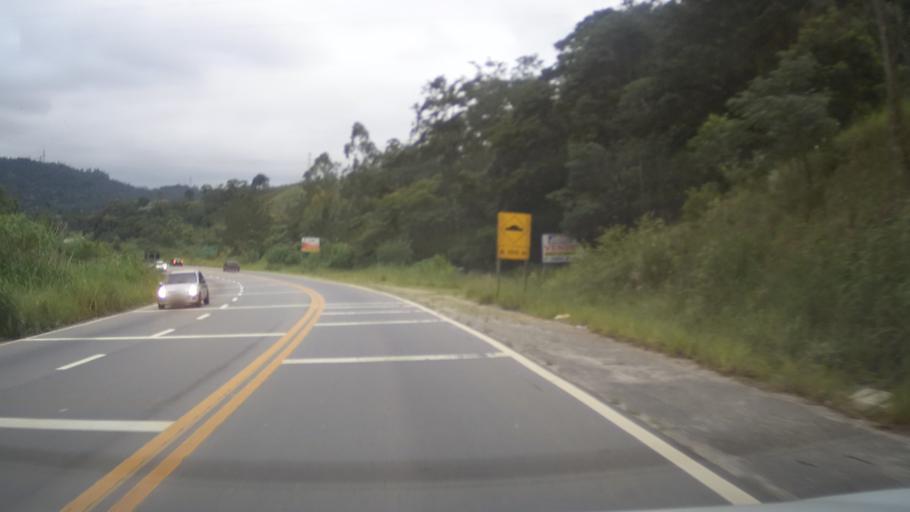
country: BR
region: Sao Paulo
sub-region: Aruja
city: Aruja
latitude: -23.3839
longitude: -46.4366
